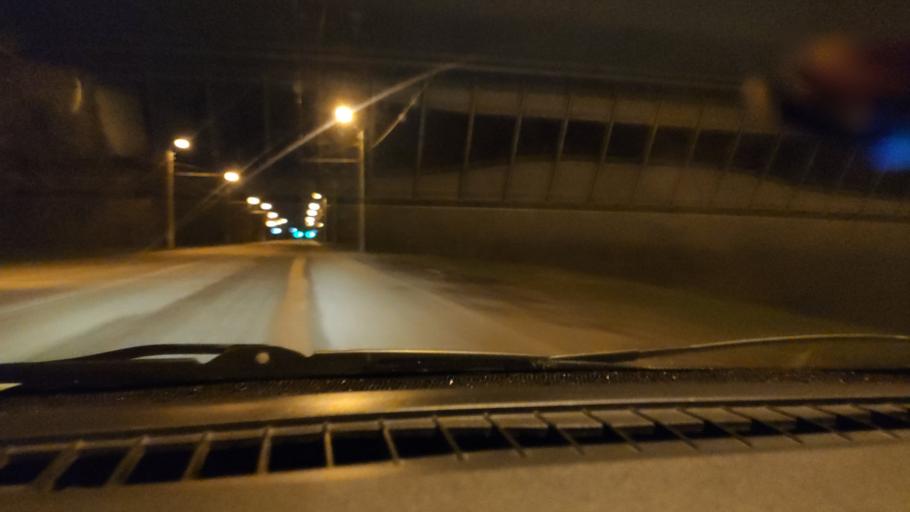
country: RU
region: Bashkortostan
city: Sterlitamak
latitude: 53.6591
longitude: 55.9234
